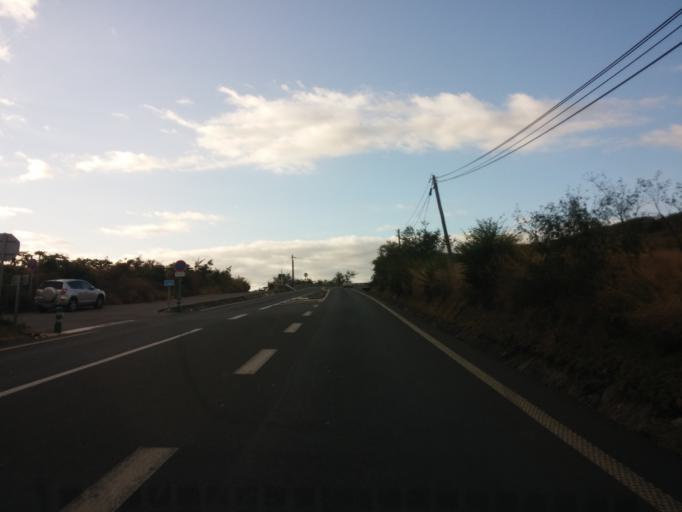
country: RE
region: Reunion
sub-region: Reunion
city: Saint-Paul
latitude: -21.0437
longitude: 55.2403
